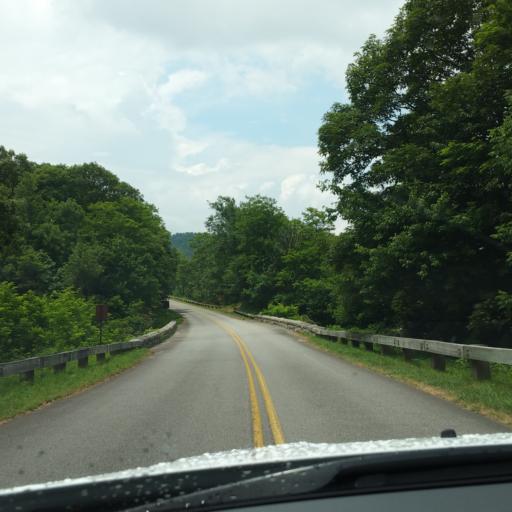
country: US
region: North Carolina
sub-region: Transylvania County
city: Brevard
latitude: 35.3739
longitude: -82.7905
